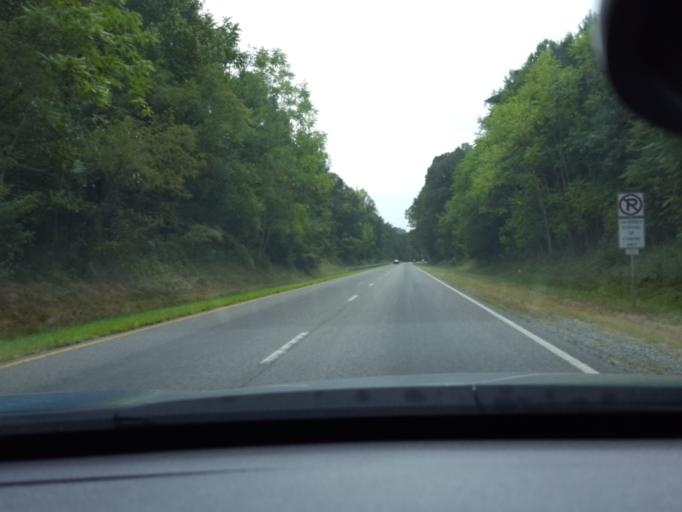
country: US
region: Virginia
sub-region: Caroline County
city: Bowling Green
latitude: 38.1268
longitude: -77.2435
